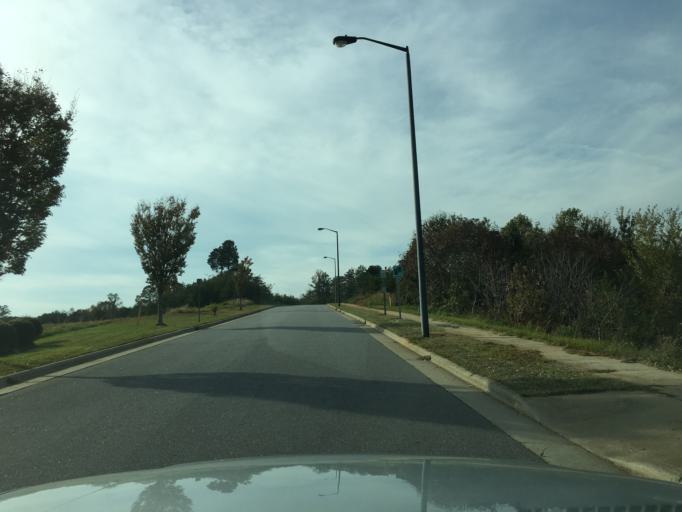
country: US
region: North Carolina
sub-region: Catawba County
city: Saint Stephens
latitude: 35.7267
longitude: -81.2852
